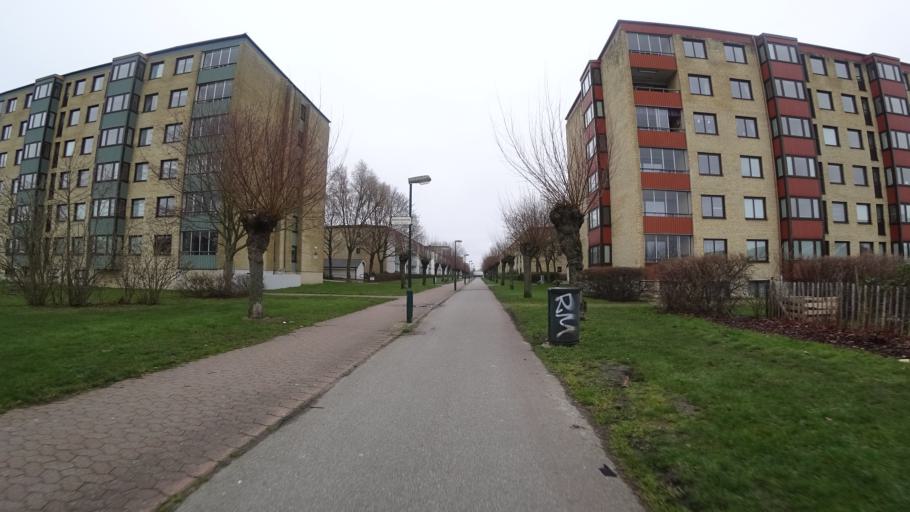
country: SE
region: Skane
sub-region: Malmo
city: Malmoe
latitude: 55.5825
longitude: 12.9740
